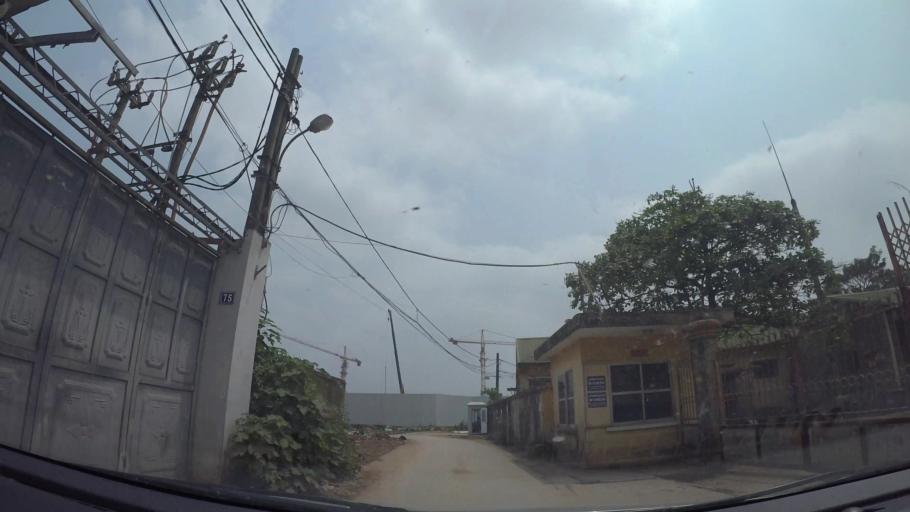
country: VN
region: Ha Noi
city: Tay Ho
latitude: 21.0859
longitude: 105.7957
